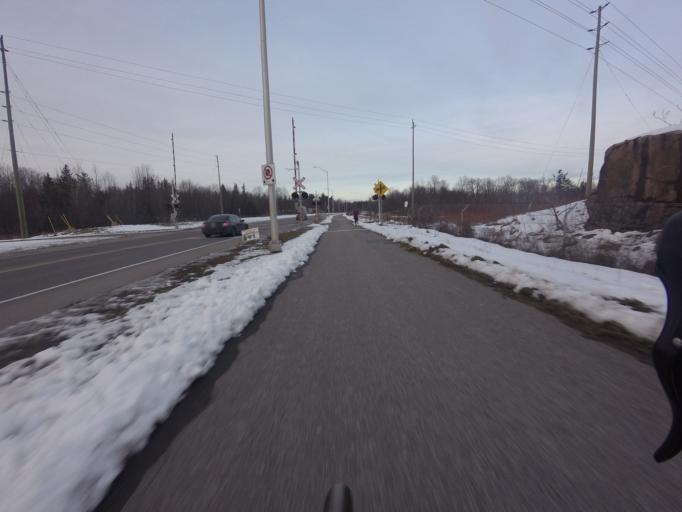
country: CA
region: Ontario
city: Bells Corners
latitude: 45.3319
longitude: -75.9495
